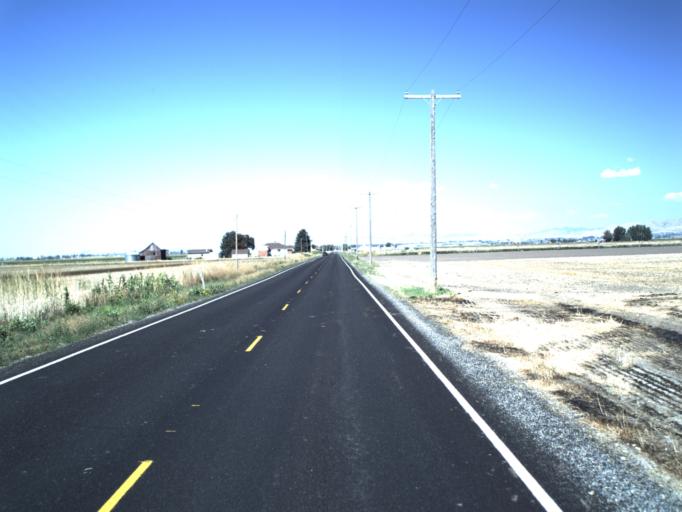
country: US
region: Utah
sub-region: Cache County
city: Lewiston
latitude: 41.9790
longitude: -111.8762
